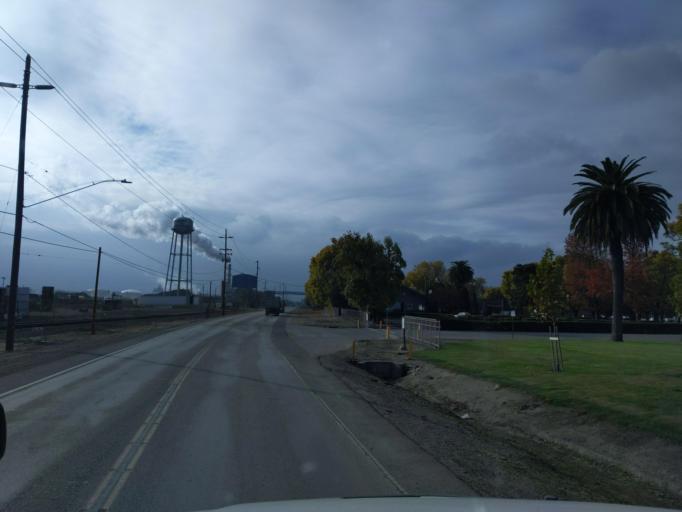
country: US
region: California
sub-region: San Joaquin County
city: Country Club
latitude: 37.9450
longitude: -121.3228
